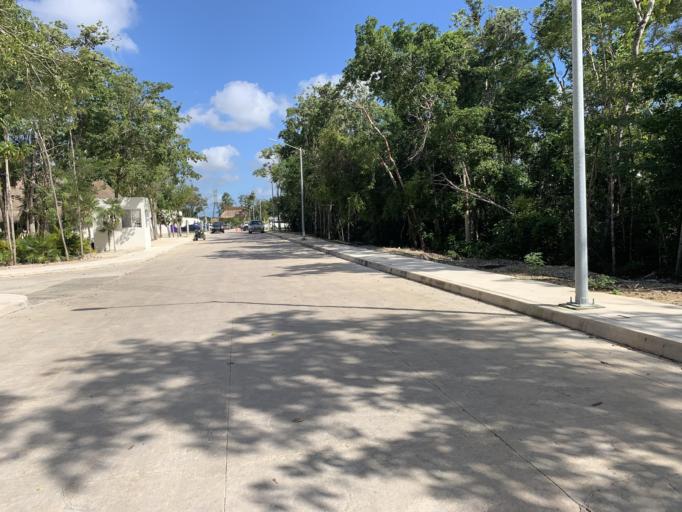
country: MX
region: Quintana Roo
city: Alfredo V. Bonfil
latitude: 20.8709
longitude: -86.9036
